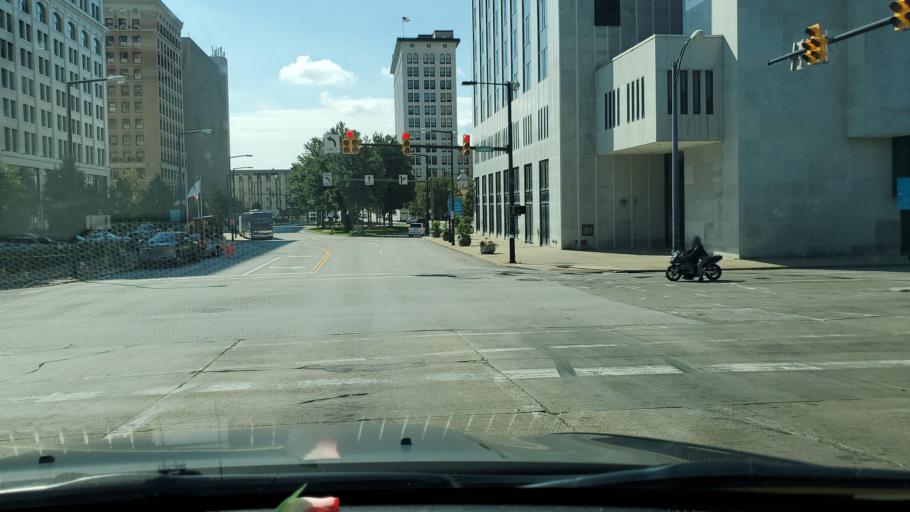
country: US
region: Ohio
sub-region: Mahoning County
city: Youngstown
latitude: 41.1012
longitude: -80.6485
